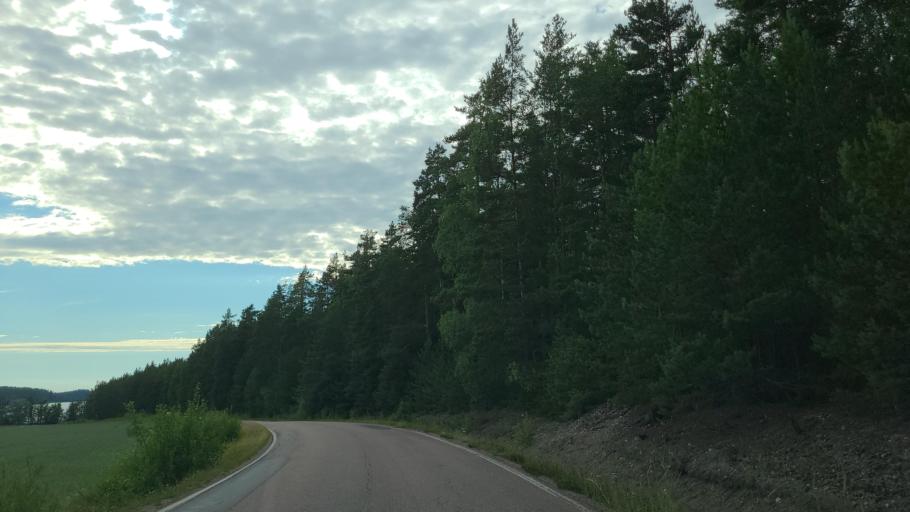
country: FI
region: Varsinais-Suomi
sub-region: Turku
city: Rymaettylae
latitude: 60.3458
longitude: 21.9694
